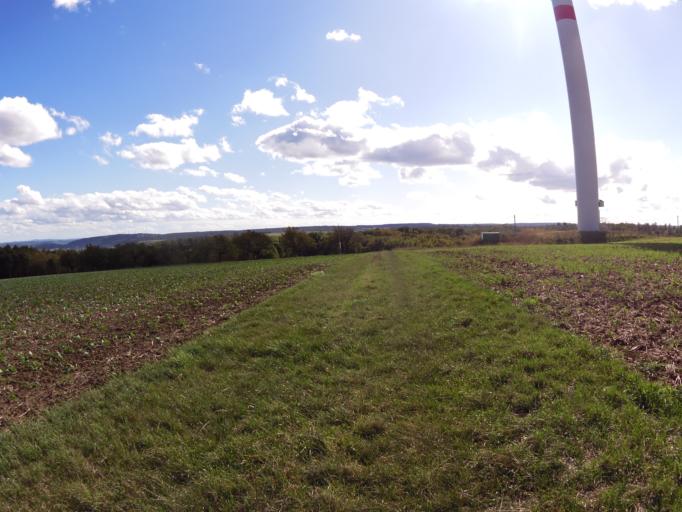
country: DE
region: Bavaria
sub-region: Regierungsbezirk Unterfranken
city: Erlabrunn
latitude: 49.8331
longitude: 9.8343
